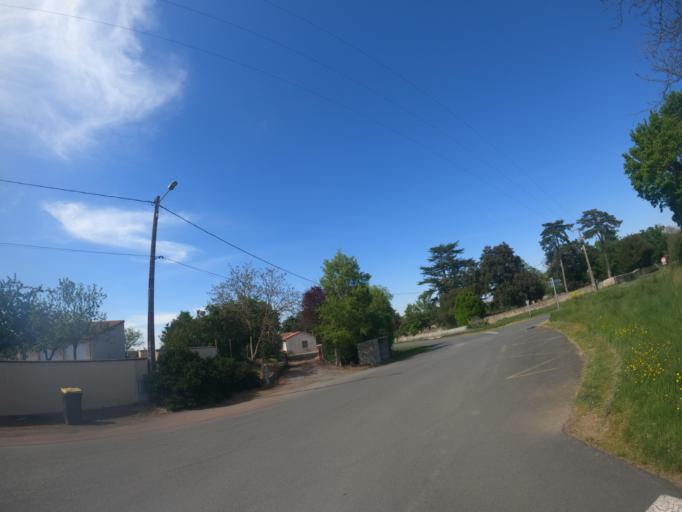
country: FR
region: Poitou-Charentes
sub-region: Departement des Deux-Sevres
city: Saint-Varent
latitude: 46.9125
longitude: -0.1906
